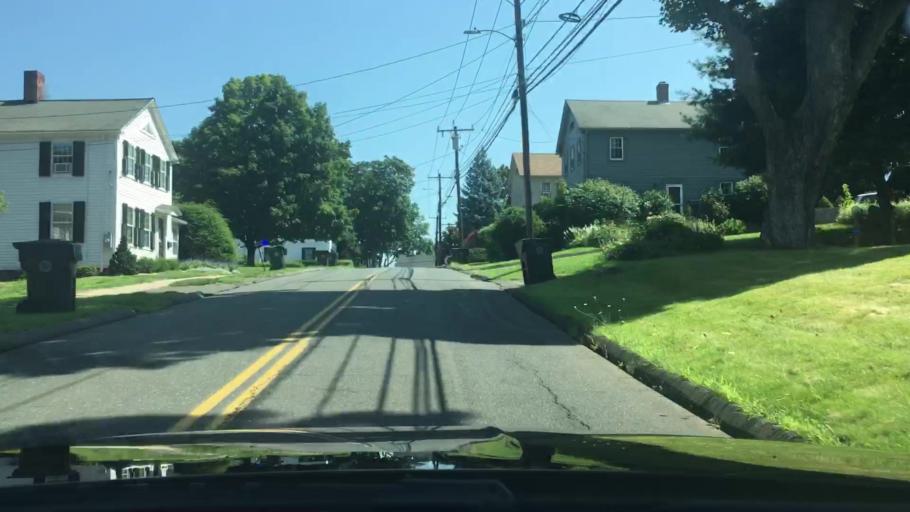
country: US
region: Connecticut
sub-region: Hartford County
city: Kensington
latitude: 41.6176
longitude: -72.7482
